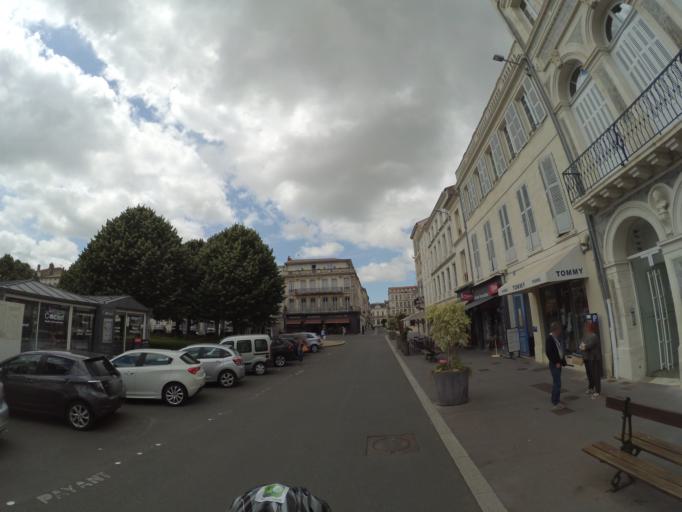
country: FR
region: Poitou-Charentes
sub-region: Departement de la Charente-Maritime
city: Rochefort
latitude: 45.9371
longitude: -0.9616
